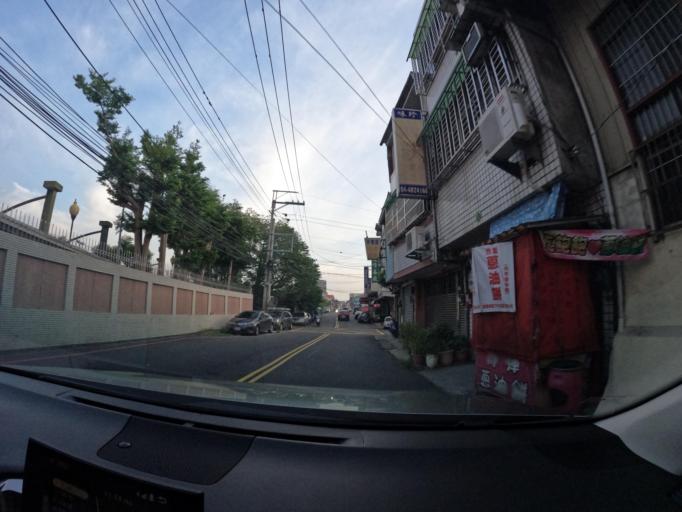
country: TW
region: Taiwan
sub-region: Taichung City
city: Taichung
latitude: 24.1184
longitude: 120.6848
